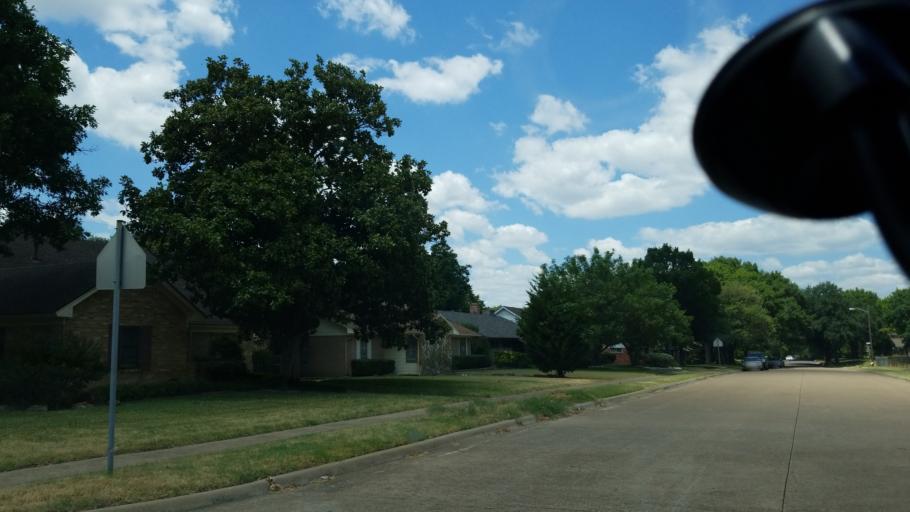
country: US
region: Texas
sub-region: Dallas County
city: Cockrell Hill
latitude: 32.6957
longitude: -96.8541
